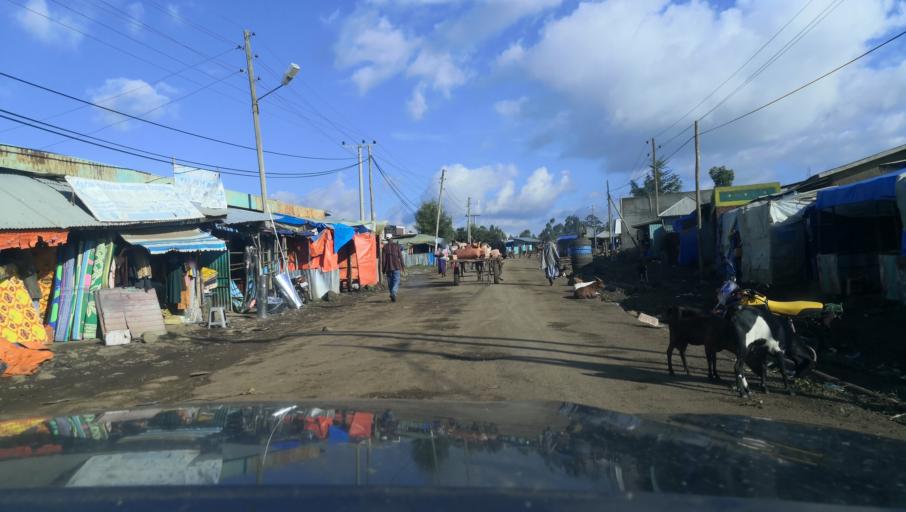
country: ET
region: Oromiya
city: Tulu Bolo
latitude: 8.4679
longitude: 38.2517
